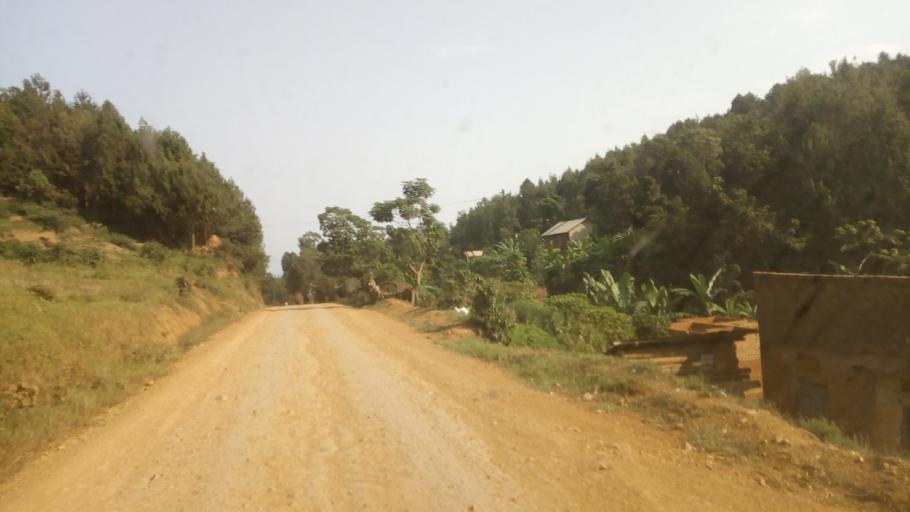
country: UG
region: Western Region
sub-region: Kanungu District
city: Ntungamo
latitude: -0.8286
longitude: 29.7082
